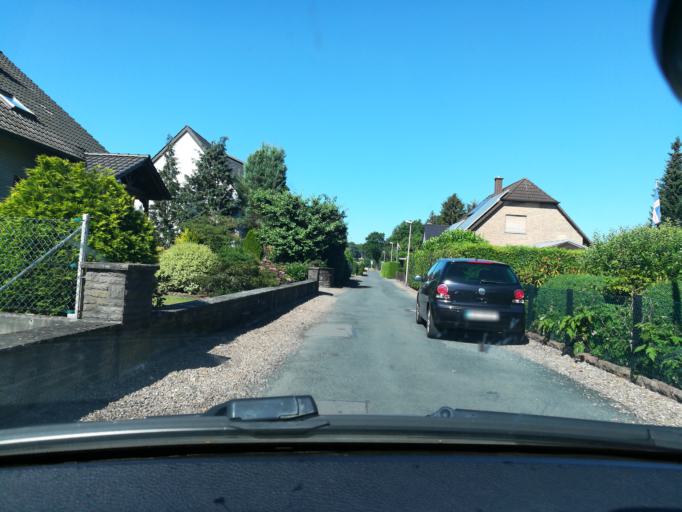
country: DE
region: North Rhine-Westphalia
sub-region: Regierungsbezirk Detmold
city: Minden
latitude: 52.3132
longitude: 8.9305
